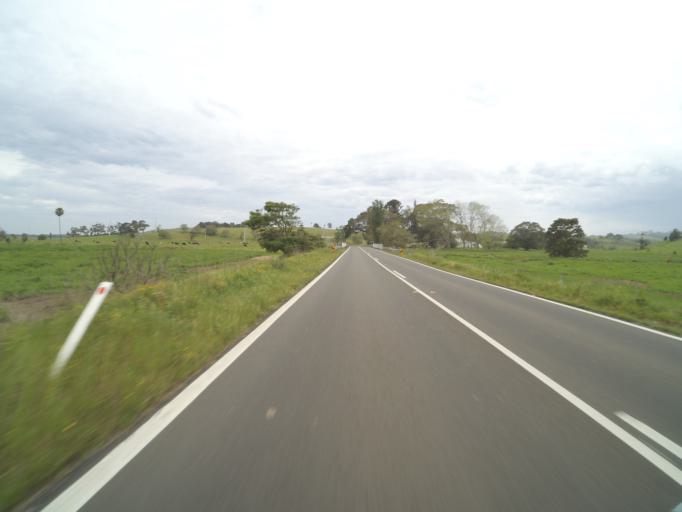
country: AU
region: New South Wales
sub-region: Kiama
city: Jamberoo
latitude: -34.6539
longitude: 150.8079
